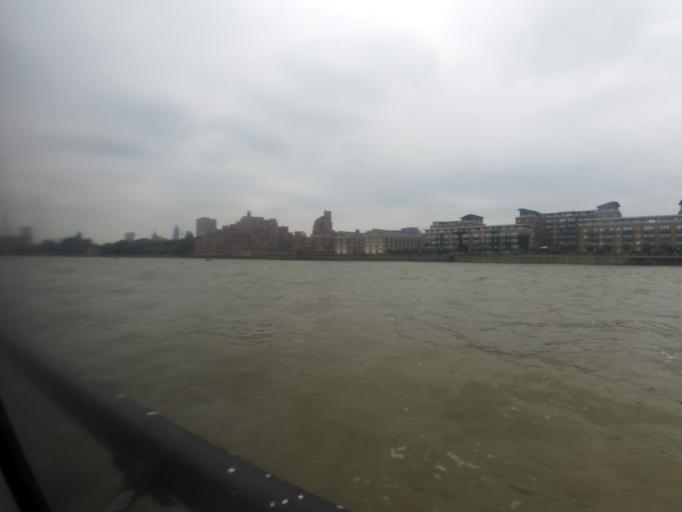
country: GB
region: England
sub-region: Greater London
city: Bethnal Green
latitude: 51.5084
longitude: -0.0424
